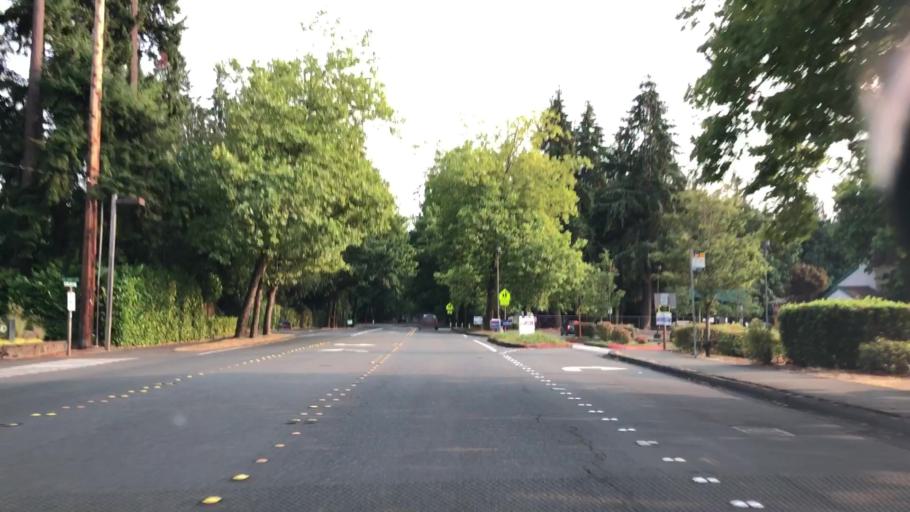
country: US
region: Washington
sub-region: King County
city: Mercer Island
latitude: 47.5542
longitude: -122.2216
